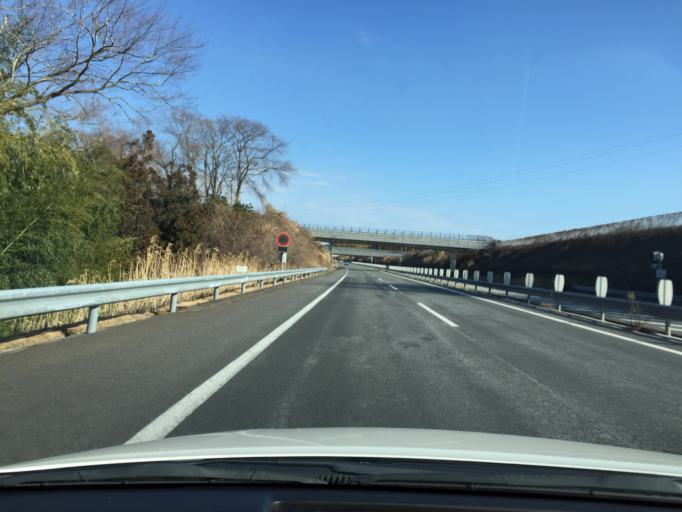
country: JP
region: Fukushima
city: Namie
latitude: 37.2997
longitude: 140.9875
